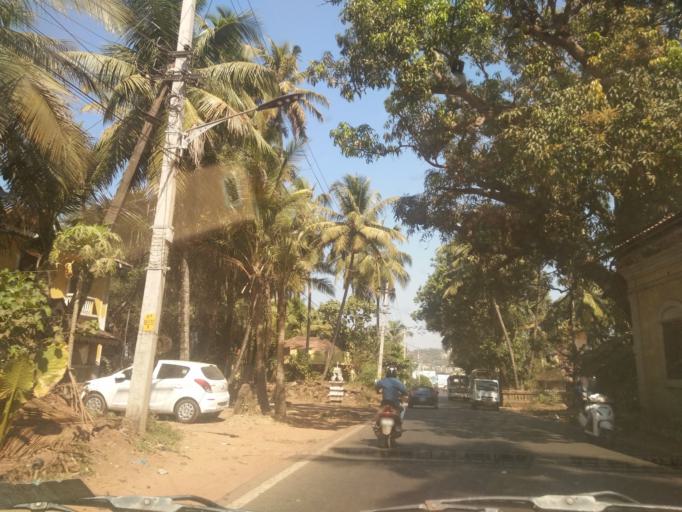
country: IN
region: Goa
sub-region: North Goa
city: Guirim
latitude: 15.5795
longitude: 73.8062
